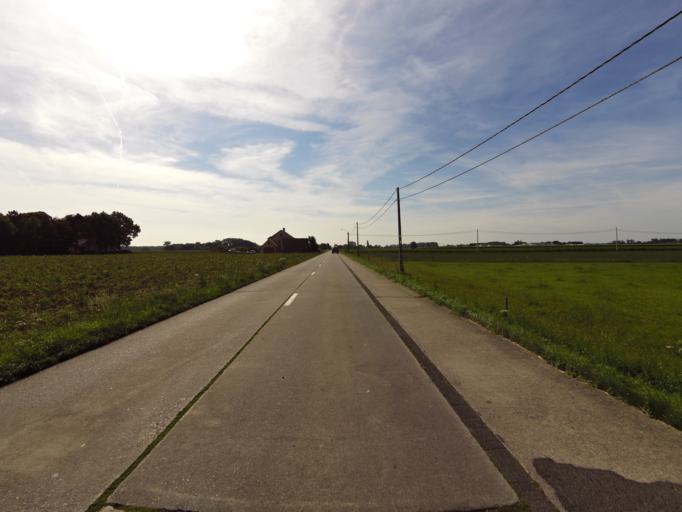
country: BE
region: Flanders
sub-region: Provincie West-Vlaanderen
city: Koekelare
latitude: 51.0677
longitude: 2.9967
